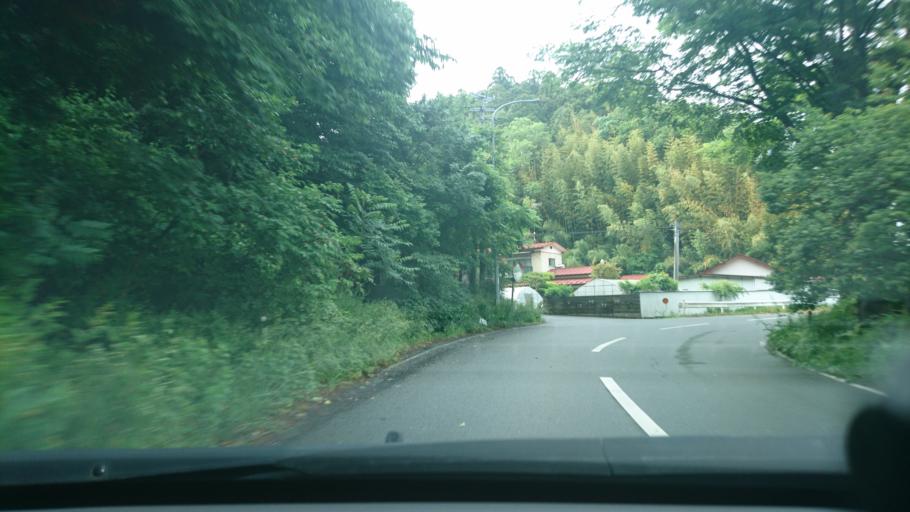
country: JP
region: Miyagi
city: Wakuya
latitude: 38.6643
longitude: 141.2837
